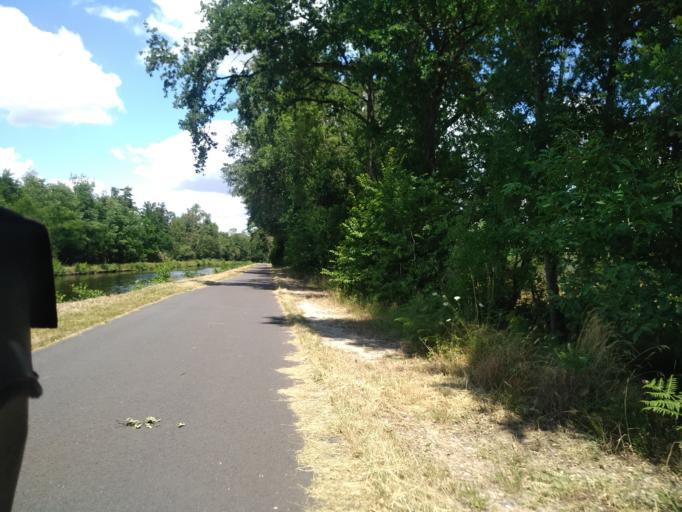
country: FR
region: Rhone-Alpes
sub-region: Departement de la Loire
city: Briennon
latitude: 46.1220
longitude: 4.0766
